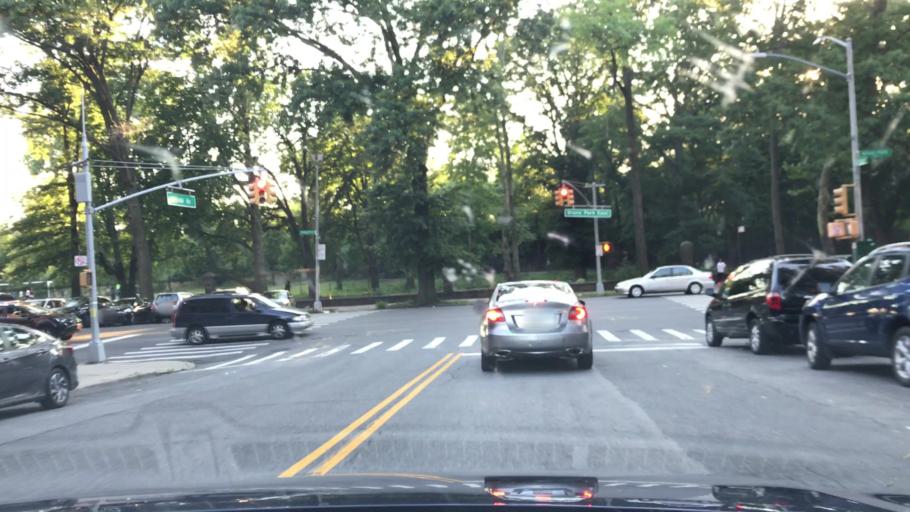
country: US
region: New York
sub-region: Bronx
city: The Bronx
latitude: 40.8679
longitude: -73.8700
